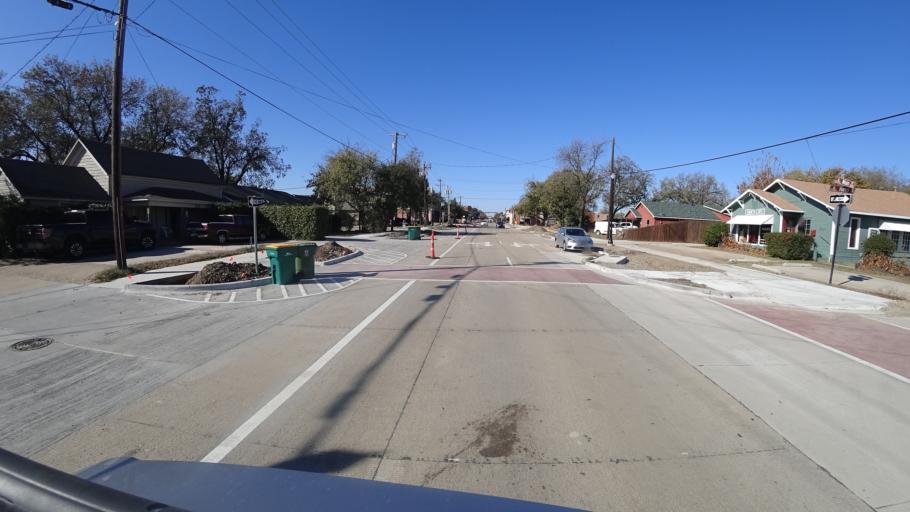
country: US
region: Texas
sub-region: Denton County
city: Lewisville
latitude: 33.0463
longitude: -96.9917
